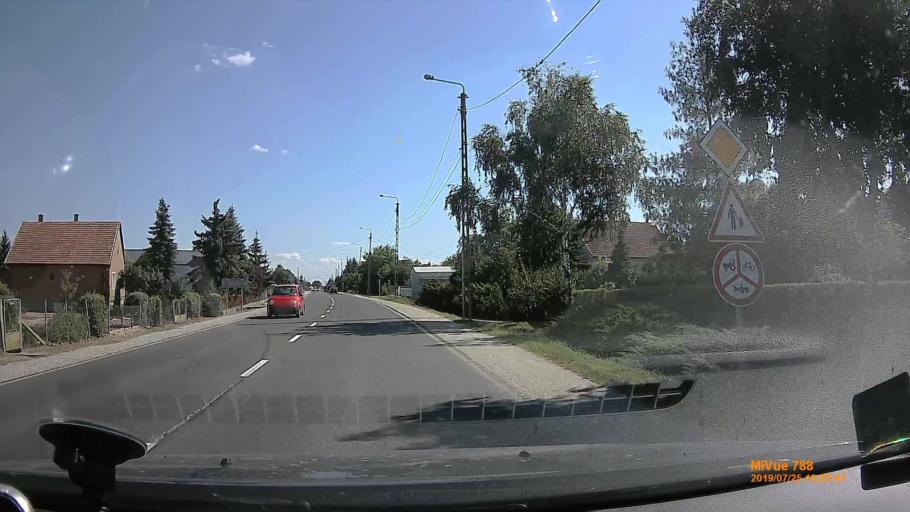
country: HU
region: Borsod-Abauj-Zemplen
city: Nyekladhaza
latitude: 47.9930
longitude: 20.8302
